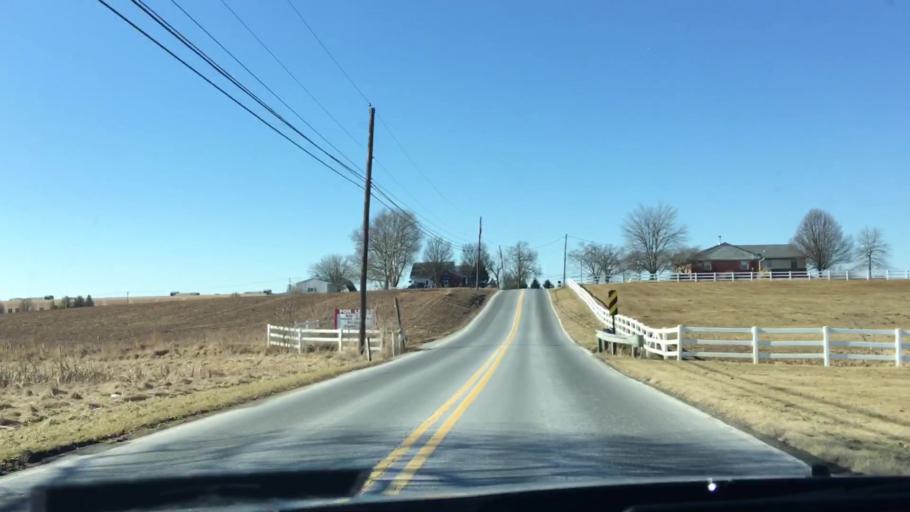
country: US
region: Pennsylvania
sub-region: Lancaster County
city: Lancaster
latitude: 40.0608
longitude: -76.2411
